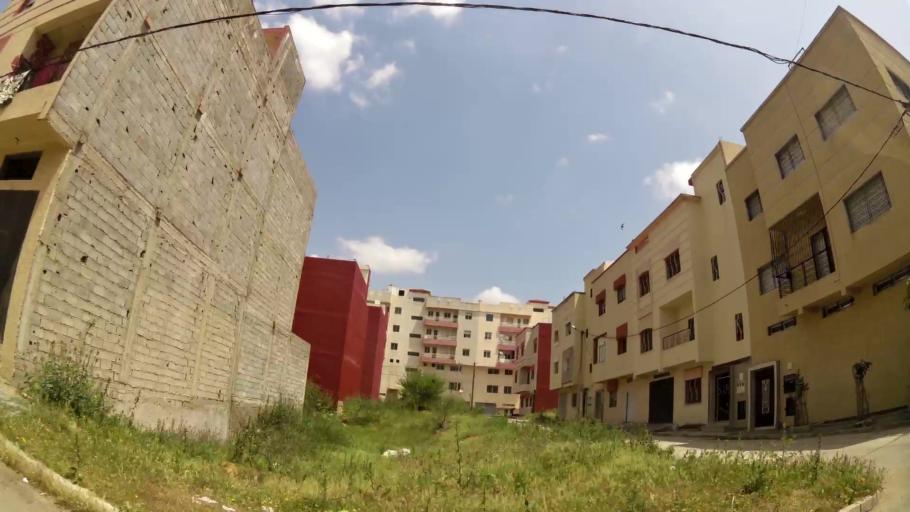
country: MA
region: Gharb-Chrarda-Beni Hssen
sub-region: Kenitra Province
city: Kenitra
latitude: 34.0114
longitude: -6.5384
